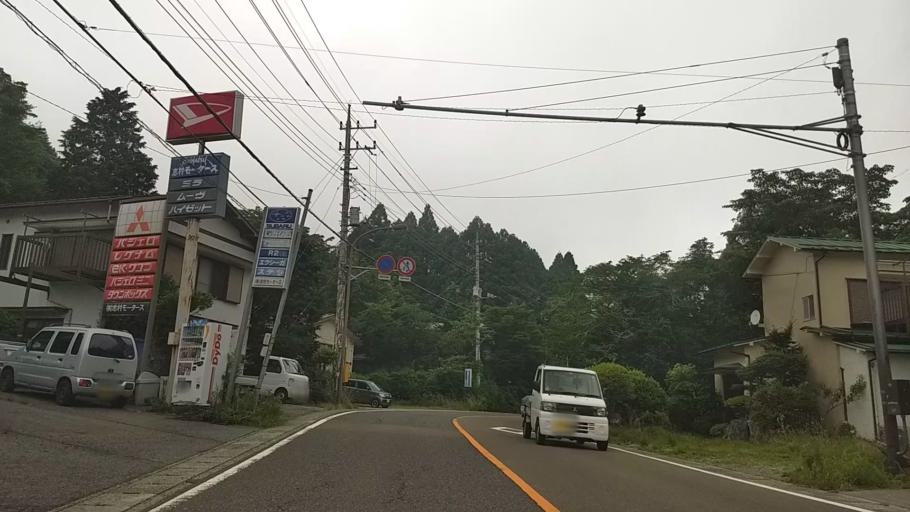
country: JP
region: Kanagawa
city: Hakone
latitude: 35.2107
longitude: 139.0368
